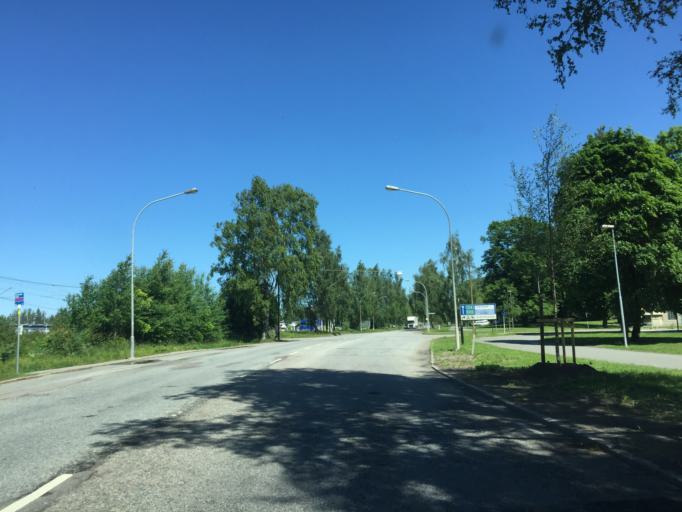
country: SE
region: OErebro
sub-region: Orebro Kommun
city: Orebro
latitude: 59.2614
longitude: 15.1925
